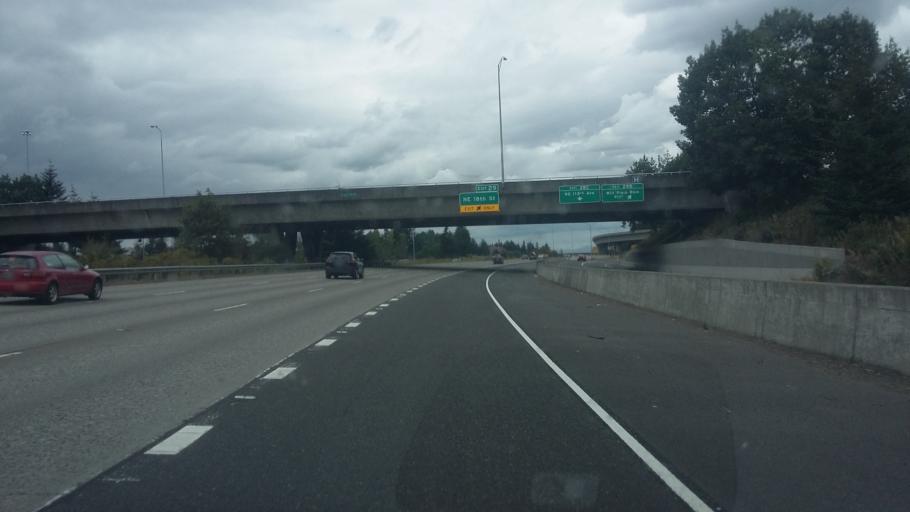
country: US
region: Washington
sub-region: Clark County
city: Orchards
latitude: 45.6200
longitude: -122.5585
